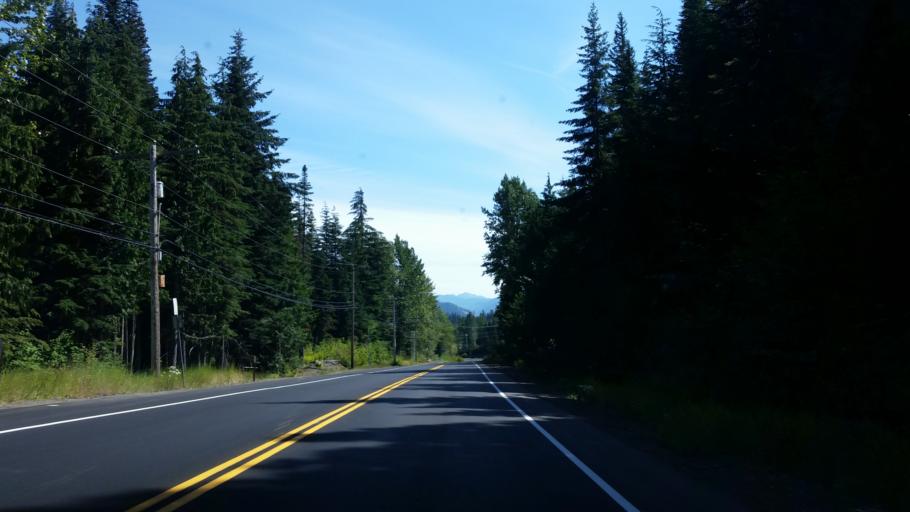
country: US
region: Washington
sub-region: King County
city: Tanner
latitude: 47.3990
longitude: -121.4014
